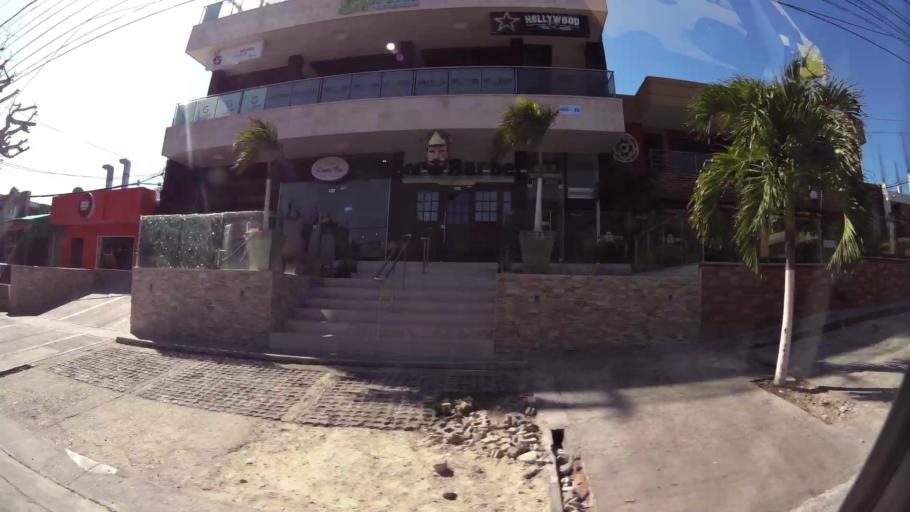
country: CO
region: Atlantico
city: Barranquilla
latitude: 11.0074
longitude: -74.8260
